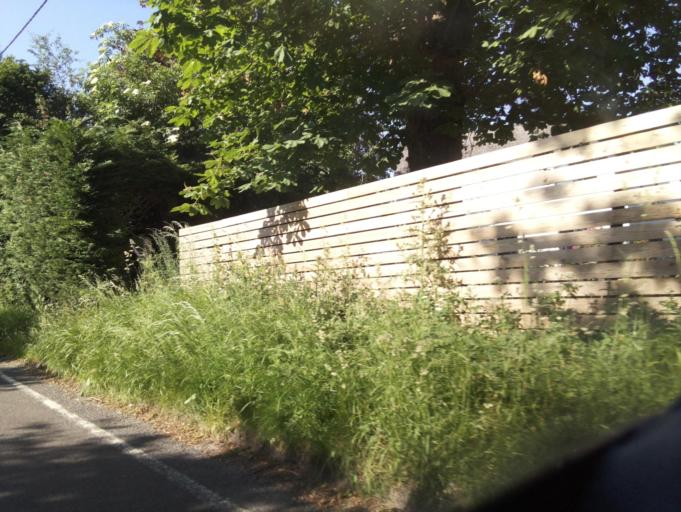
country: GB
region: England
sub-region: Hampshire
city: Winchester
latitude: 51.0837
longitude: -1.3462
